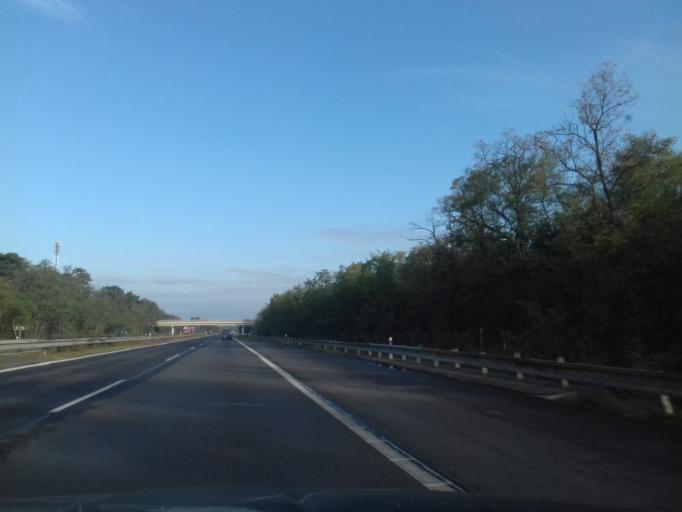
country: SK
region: Bratislavsky
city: Stupava
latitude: 48.3455
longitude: 17.0225
